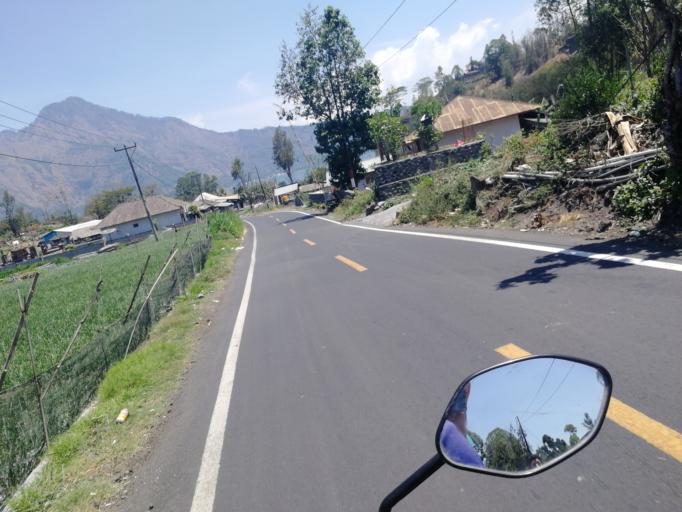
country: ID
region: Bali
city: Banjar Trunyan
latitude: -8.2356
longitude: 115.4058
